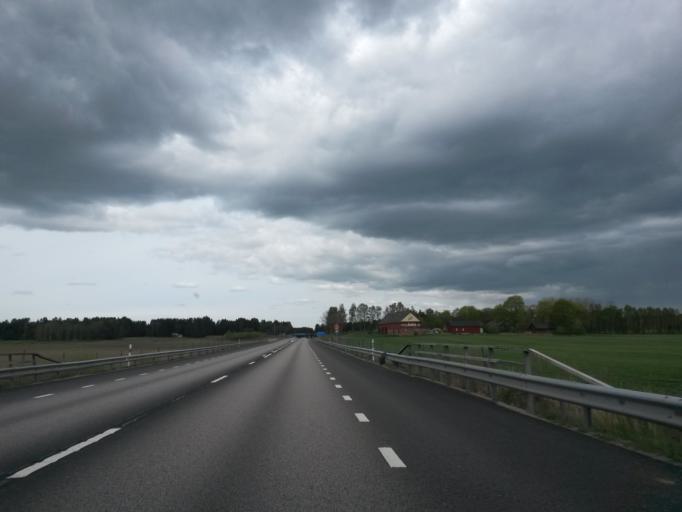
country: SE
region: Vaestra Goetaland
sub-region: Vara Kommun
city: Vara
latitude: 58.1676
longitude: 12.8870
